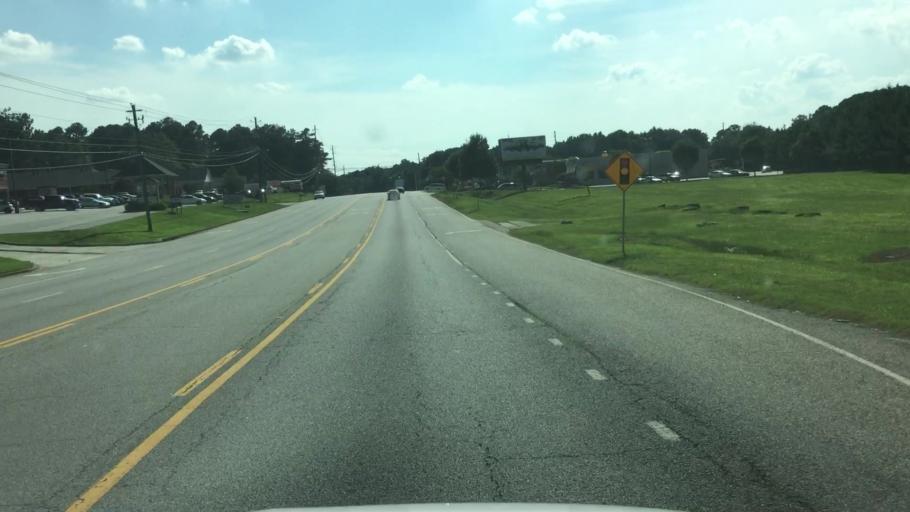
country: US
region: Georgia
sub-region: Barrow County
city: Auburn
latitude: 34.0104
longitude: -83.8498
